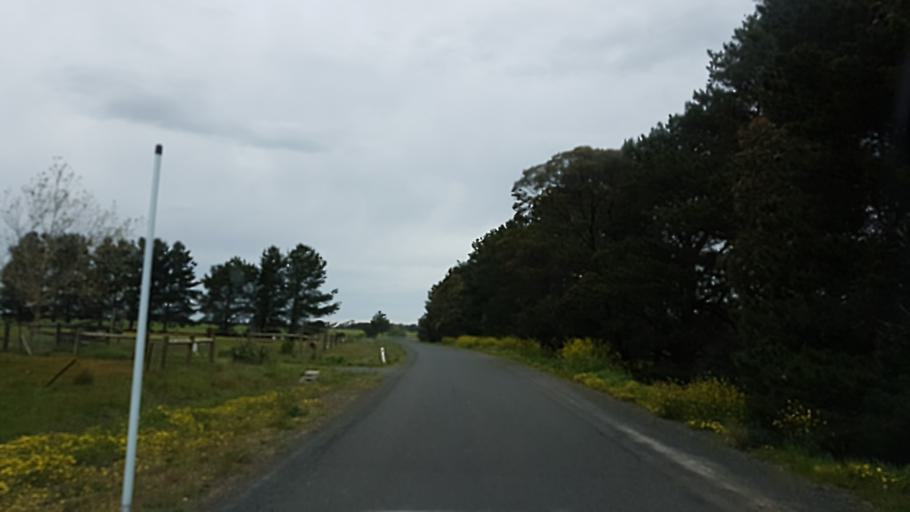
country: AU
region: Victoria
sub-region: Ballarat North
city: Mount Clear
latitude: -37.7743
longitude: 144.0895
